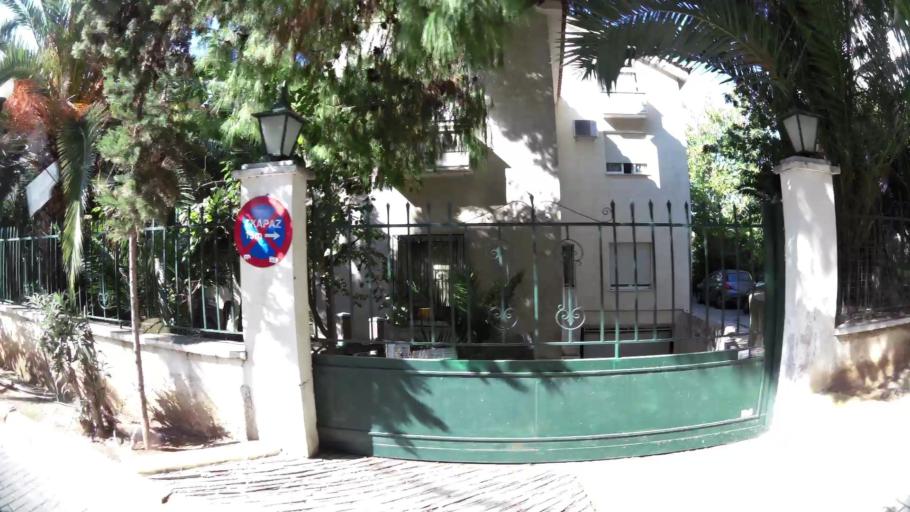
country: GR
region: Attica
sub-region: Nomarchia Athinas
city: Metamorfosi
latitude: 38.0625
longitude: 23.7734
